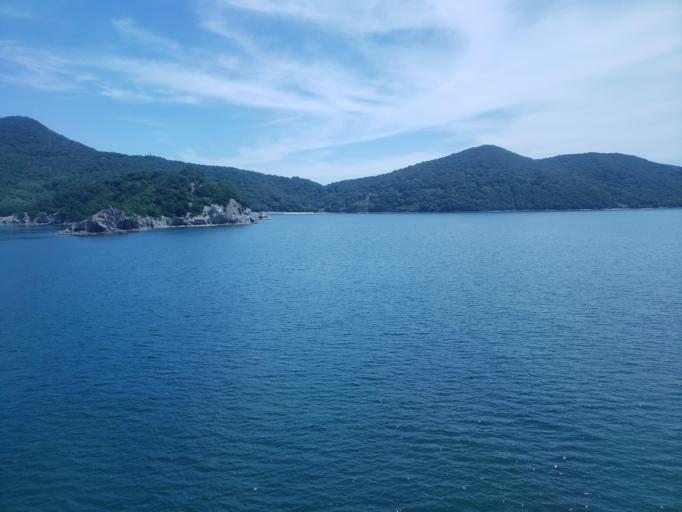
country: JP
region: Kagawa
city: Tonosho
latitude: 34.4443
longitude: 134.3164
